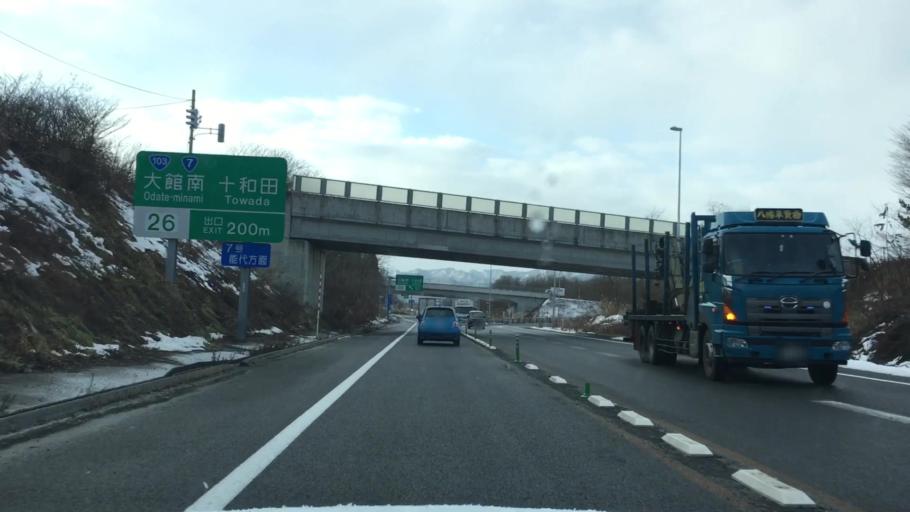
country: JP
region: Akita
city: Odate
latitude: 40.2730
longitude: 140.5321
